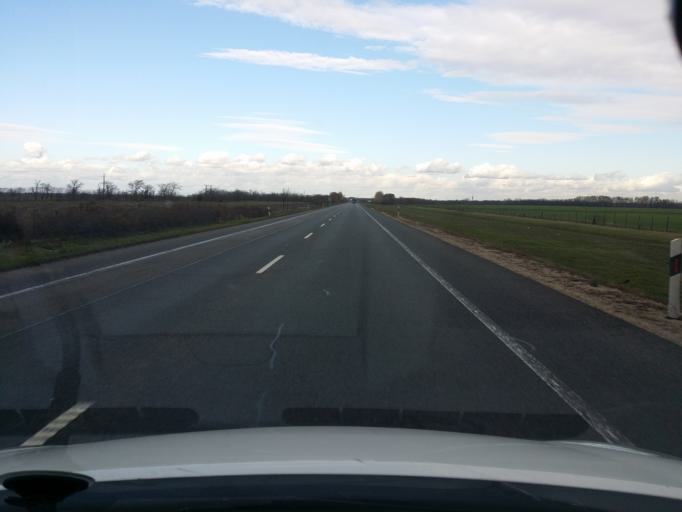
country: HU
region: Gyor-Moson-Sopron
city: Rajka
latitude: 47.9667
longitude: 17.1744
